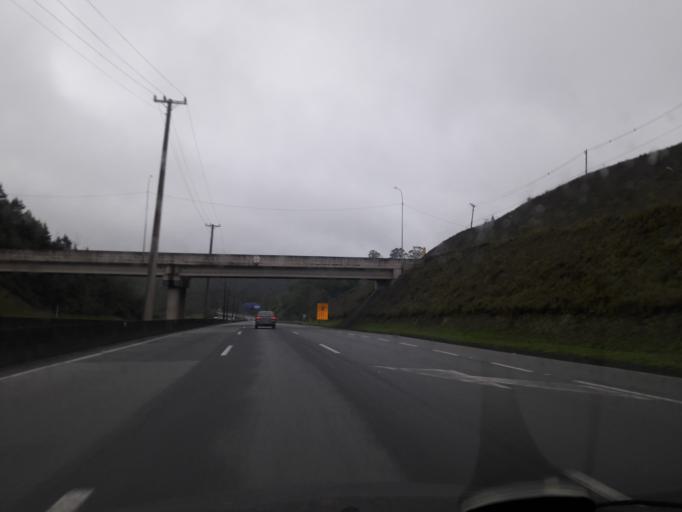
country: BR
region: Sao Paulo
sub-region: Sao Lourenco Da Serra
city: Sao Lourenco da Serra
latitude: -23.8023
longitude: -46.9175
